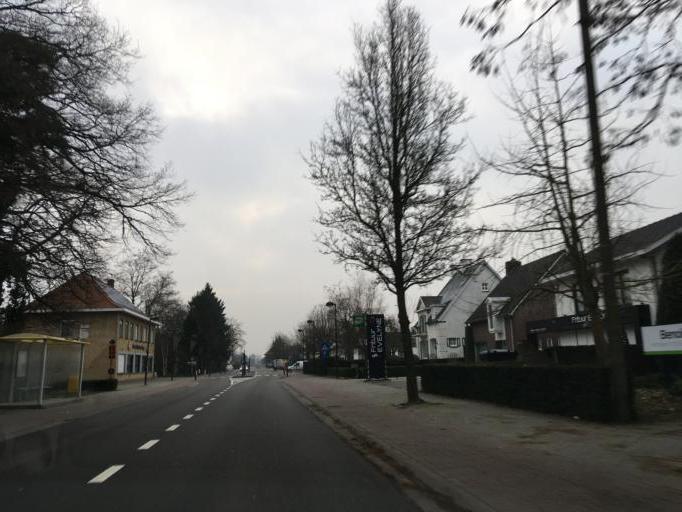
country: BE
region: Flanders
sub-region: Provincie West-Vlaanderen
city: Wielsbeke
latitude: 50.9106
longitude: 3.3717
